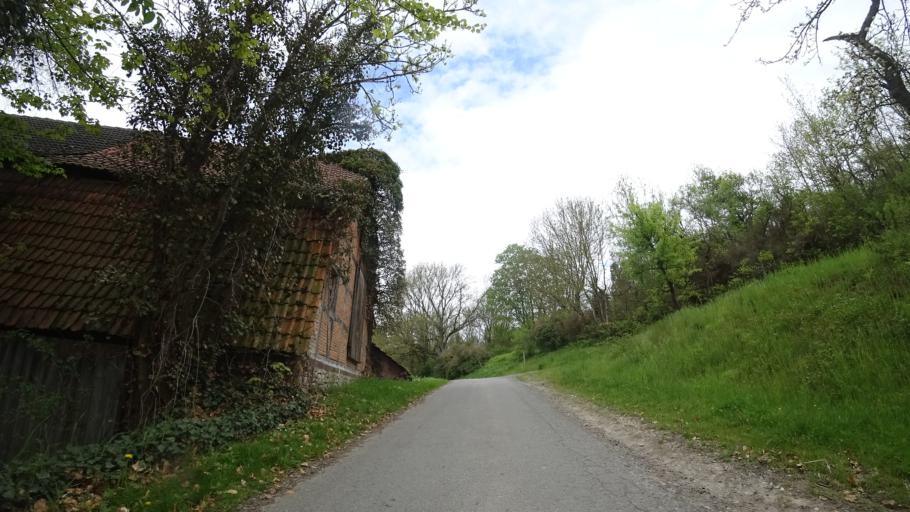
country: DE
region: Hesse
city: Liebenau
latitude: 51.4611
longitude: 9.3129
